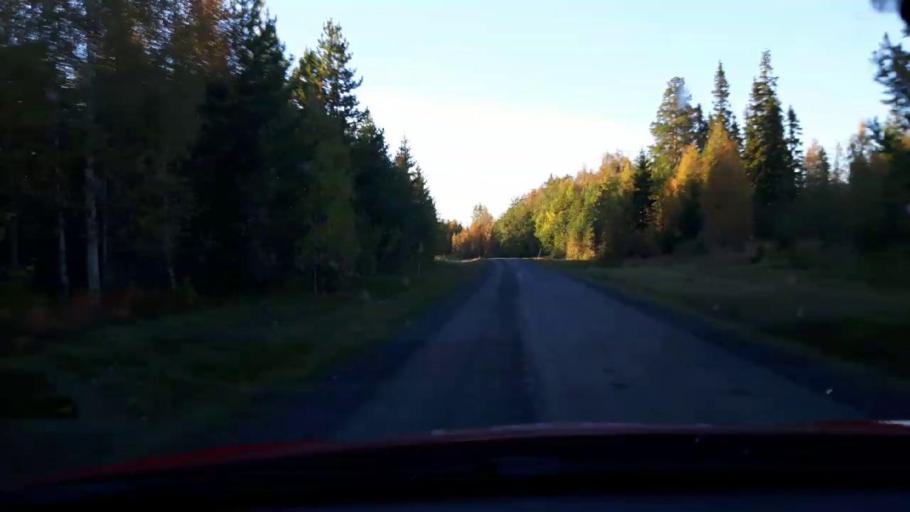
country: SE
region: Jaemtland
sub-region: Krokoms Kommun
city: Krokom
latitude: 63.4357
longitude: 14.6064
